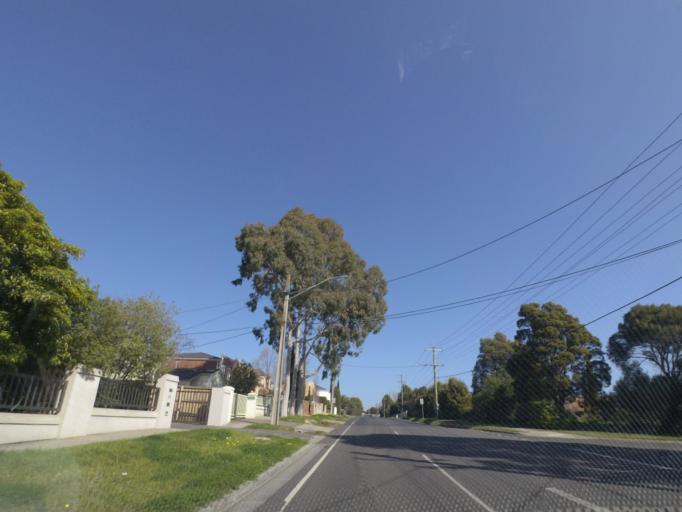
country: AU
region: Victoria
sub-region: Manningham
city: Doncaster East
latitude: -37.7705
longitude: 145.1557
